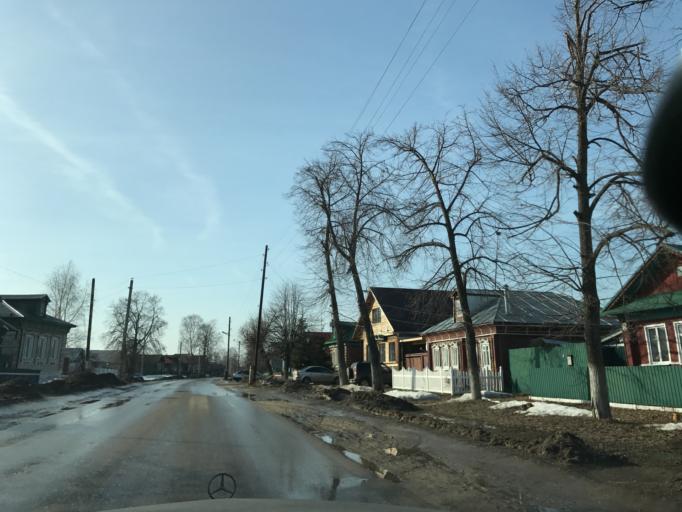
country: RU
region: Nizjnij Novgorod
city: Pavlovo
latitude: 55.9964
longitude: 43.0376
